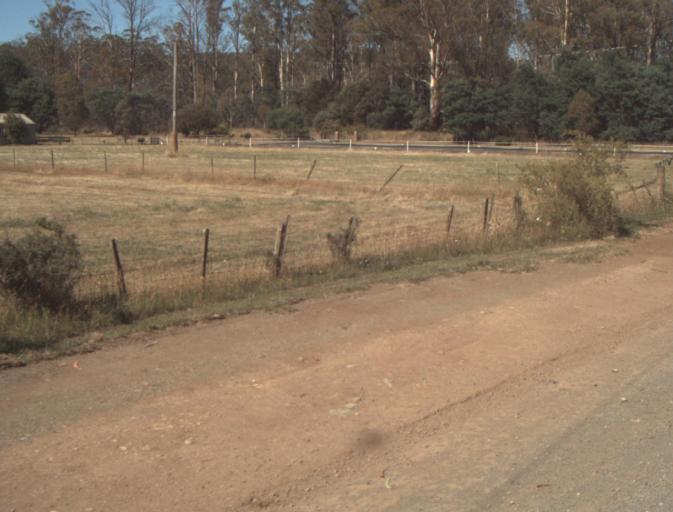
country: AU
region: Tasmania
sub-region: Launceston
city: Newstead
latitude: -41.3666
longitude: 147.2457
